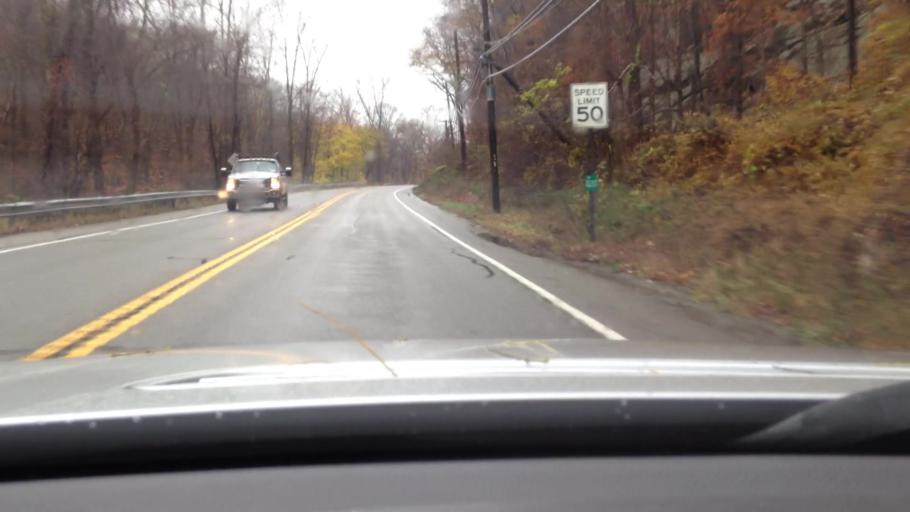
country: US
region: New York
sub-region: Westchester County
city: Peekskill
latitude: 41.3225
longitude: -73.9291
